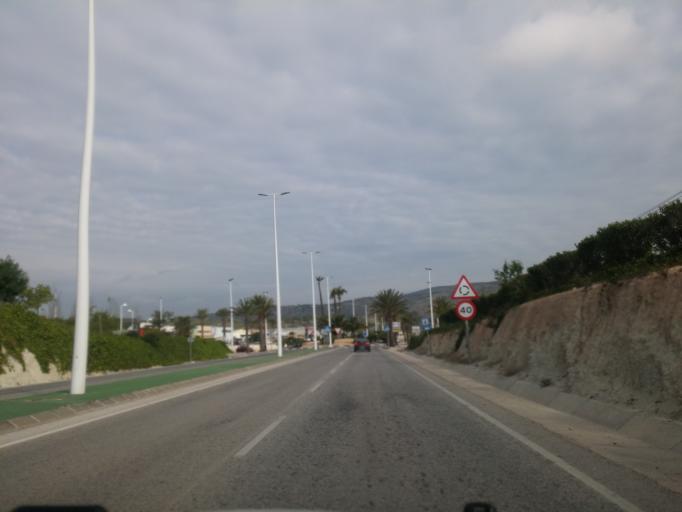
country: ES
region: Valencia
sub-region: Provincia de Alicante
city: Teulada
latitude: 38.7280
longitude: 0.0955
